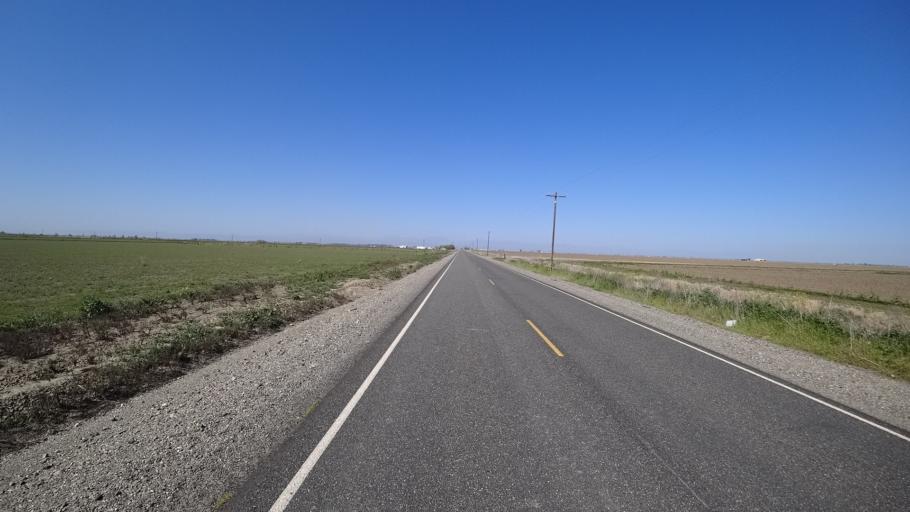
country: US
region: California
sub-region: Glenn County
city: Willows
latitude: 39.4577
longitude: -122.0600
